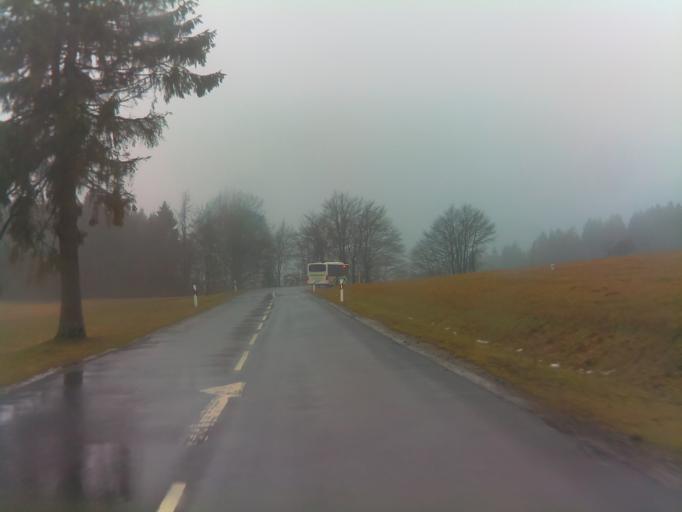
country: DE
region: Thuringia
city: Masserberg
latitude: 50.5092
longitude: 10.9170
